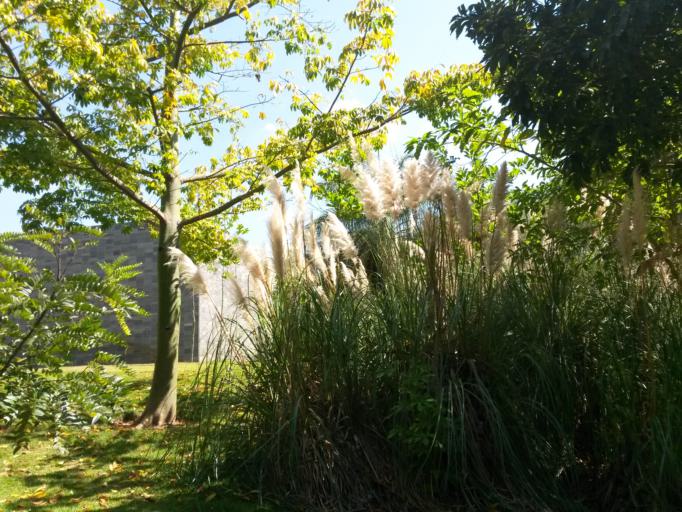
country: BR
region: Minas Gerais
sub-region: Brumadinho
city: Brumadinho
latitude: -20.1223
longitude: -44.2225
